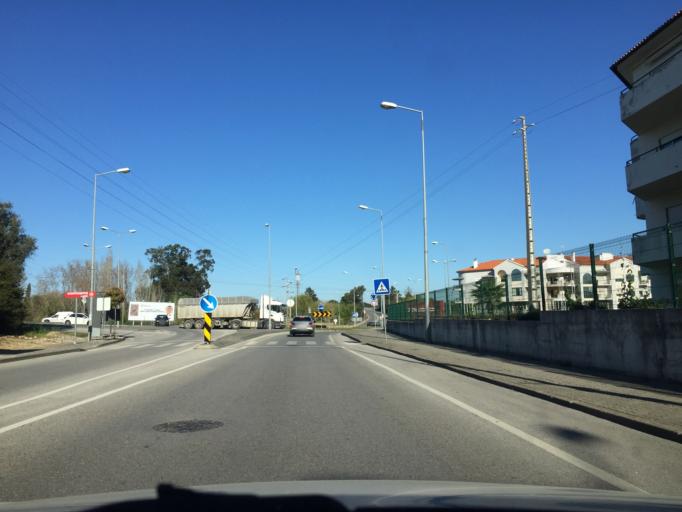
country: PT
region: Aveiro
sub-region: Anadia
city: Arcos
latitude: 40.4432
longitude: -8.4513
